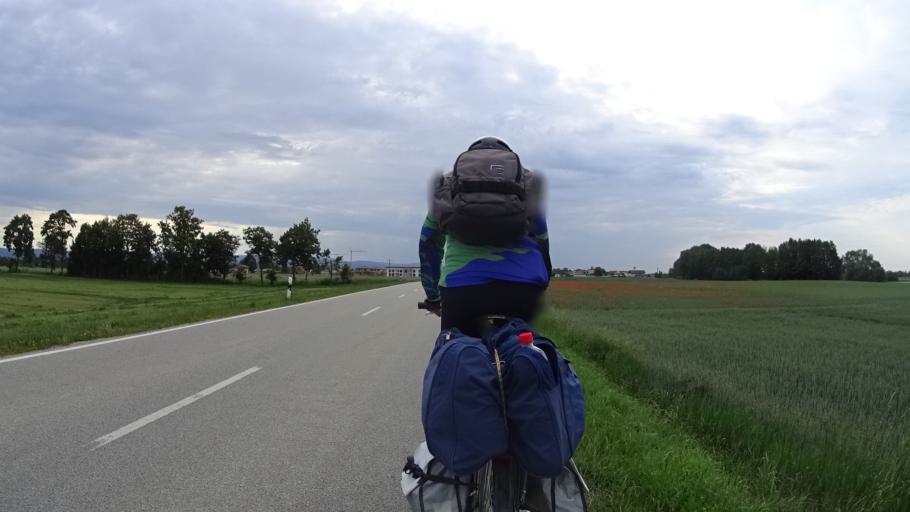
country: DE
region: Bavaria
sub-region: Lower Bavaria
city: Parkstetten
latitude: 48.9195
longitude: 12.5807
